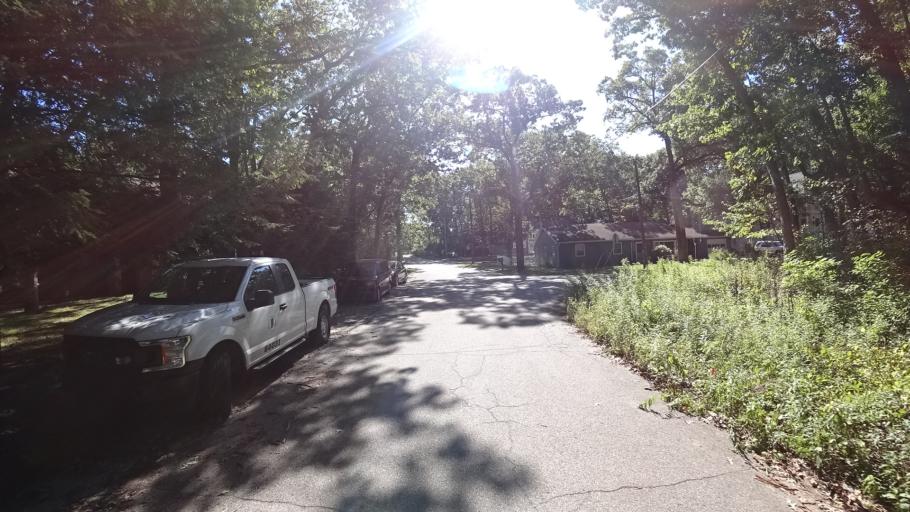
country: US
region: Indiana
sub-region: LaPorte County
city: Long Beach
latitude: 41.7520
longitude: -86.8355
